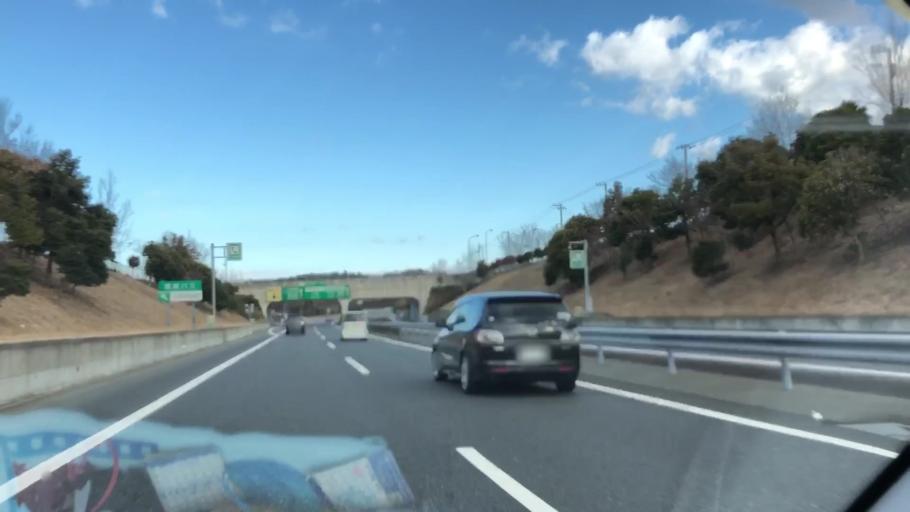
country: JP
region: Chiba
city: Kisarazu
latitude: 35.3448
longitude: 139.9444
